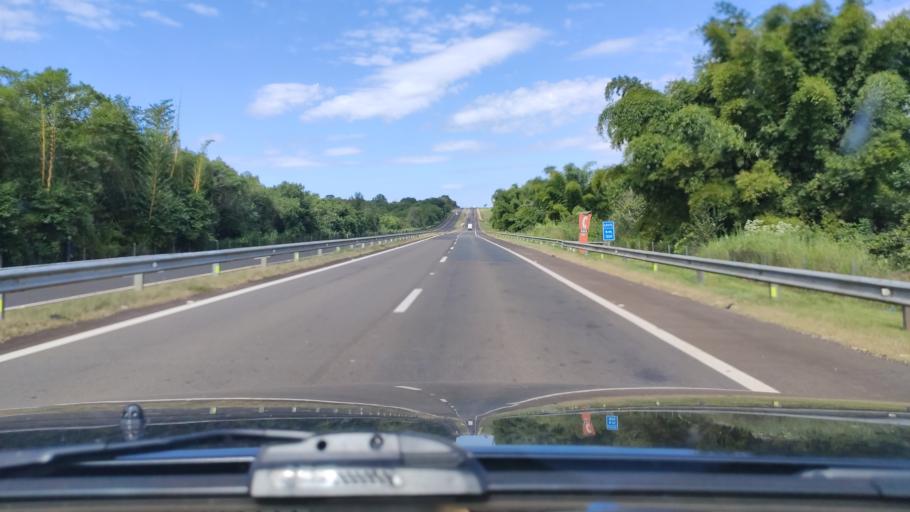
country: BR
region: Sao Paulo
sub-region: Rancharia
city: Rancharia
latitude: -22.4888
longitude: -50.9166
